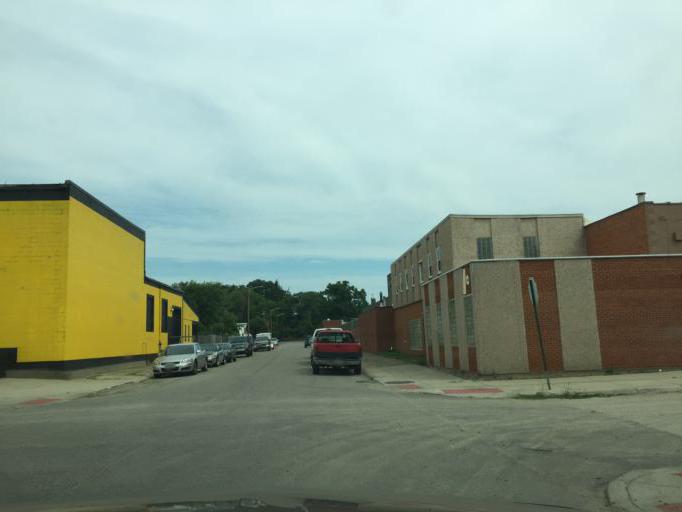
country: US
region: Michigan
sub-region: Wayne County
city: Redford
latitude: 42.4036
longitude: -83.2753
